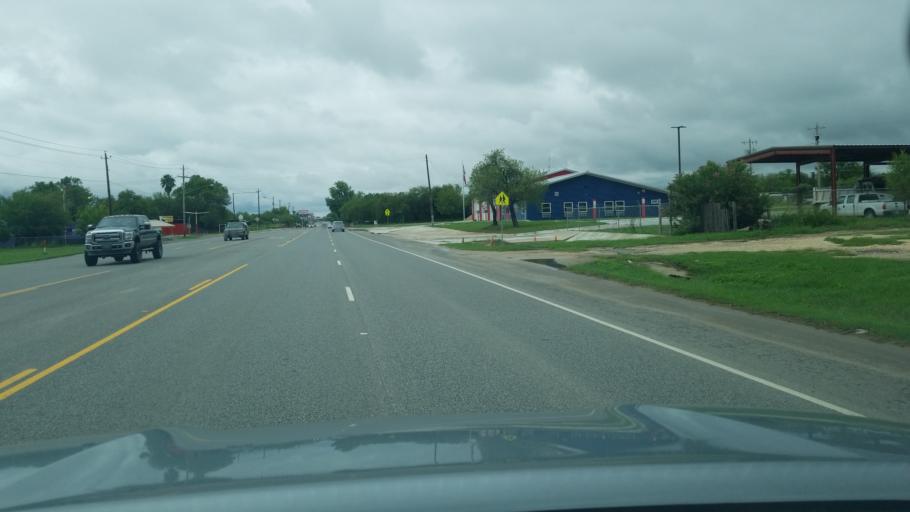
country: US
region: Texas
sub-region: Dimmit County
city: Carrizo Springs
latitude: 28.5321
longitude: -99.8527
